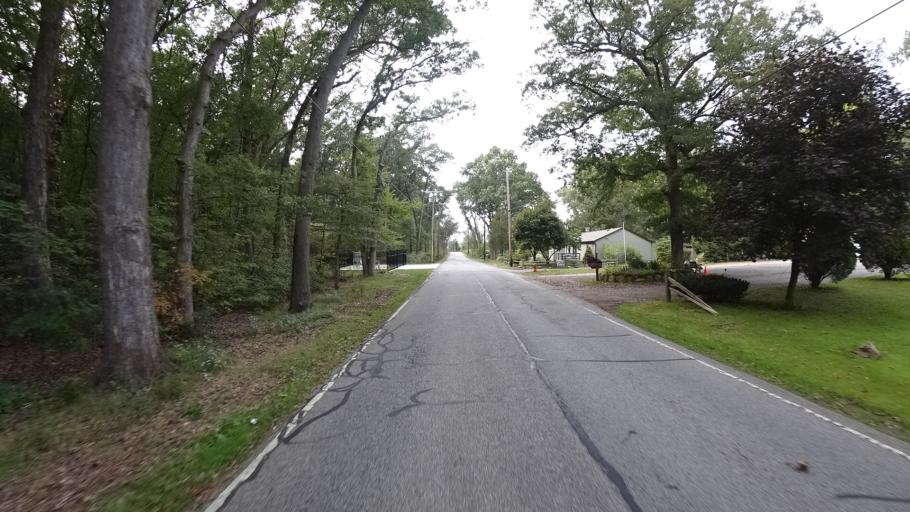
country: US
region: Indiana
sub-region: LaPorte County
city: Long Beach
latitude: 41.7277
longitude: -86.8654
